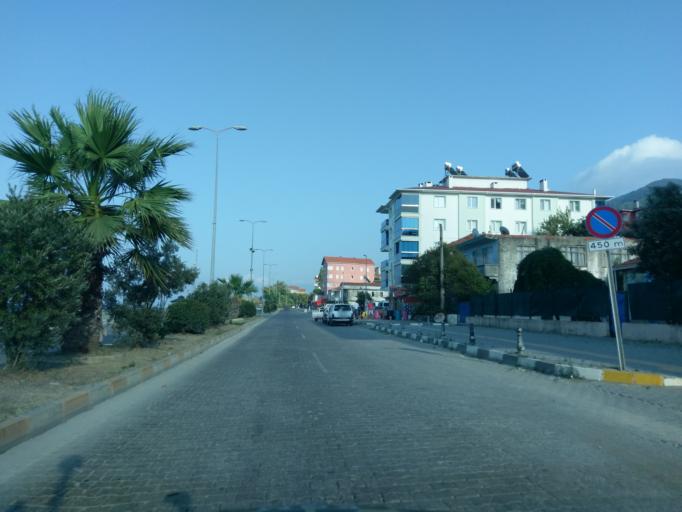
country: TR
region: Kastamonu
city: Catalzeytin
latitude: 41.9539
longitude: 34.2199
